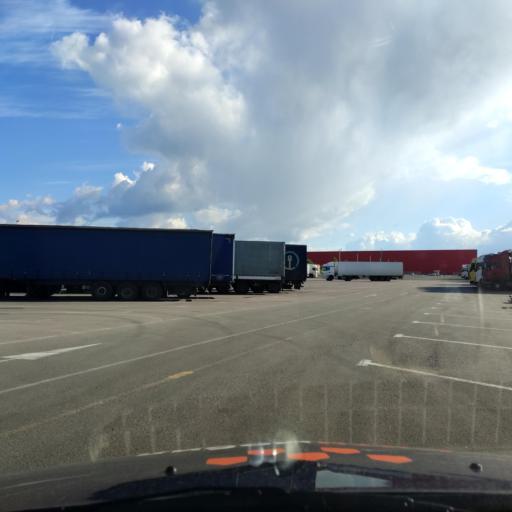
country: RU
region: Voronezj
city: Podgornoye
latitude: 51.8061
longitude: 39.2207
